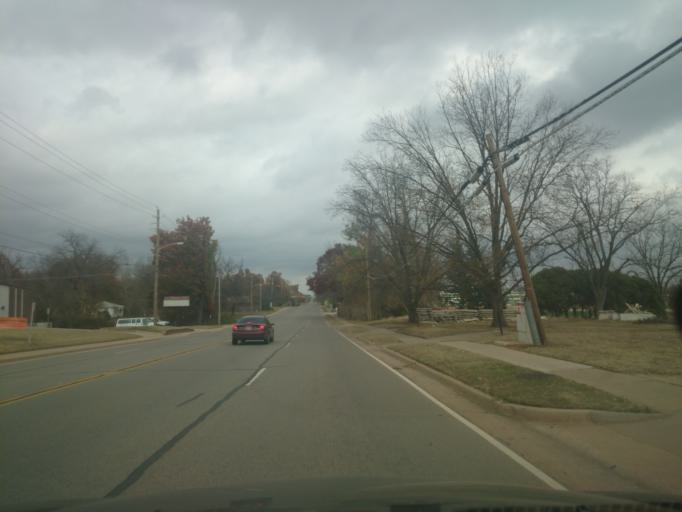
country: US
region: Oklahoma
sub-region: Payne County
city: Stillwater
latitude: 36.1316
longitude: -97.0694
